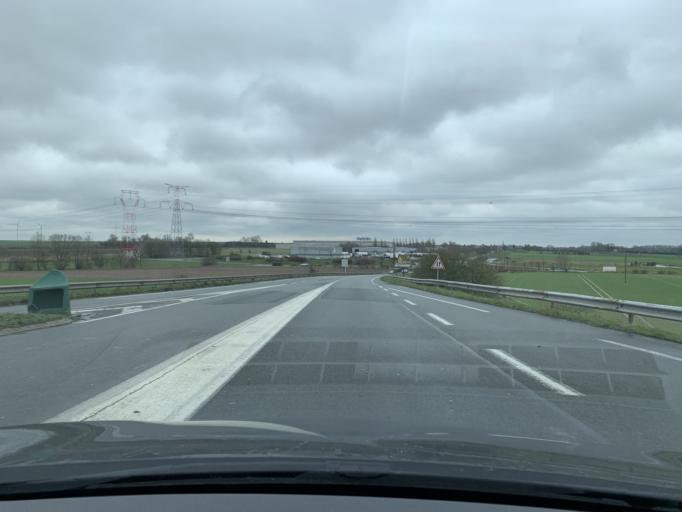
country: FR
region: Nord-Pas-de-Calais
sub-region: Departement du Nord
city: Hordain
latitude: 50.2524
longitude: 3.3220
